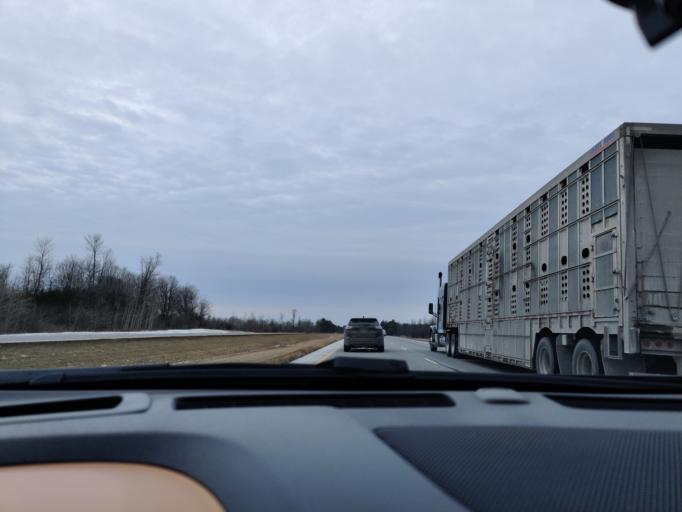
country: US
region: New York
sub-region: St. Lawrence County
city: Ogdensburg
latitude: 44.8378
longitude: -75.3622
